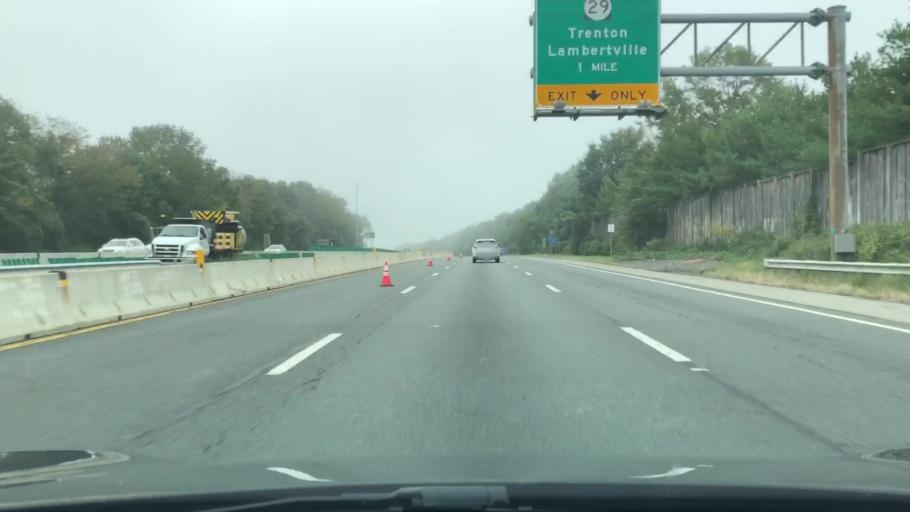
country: US
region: Pennsylvania
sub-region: Bucks County
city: Yardley
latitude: 40.2725
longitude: -74.8335
